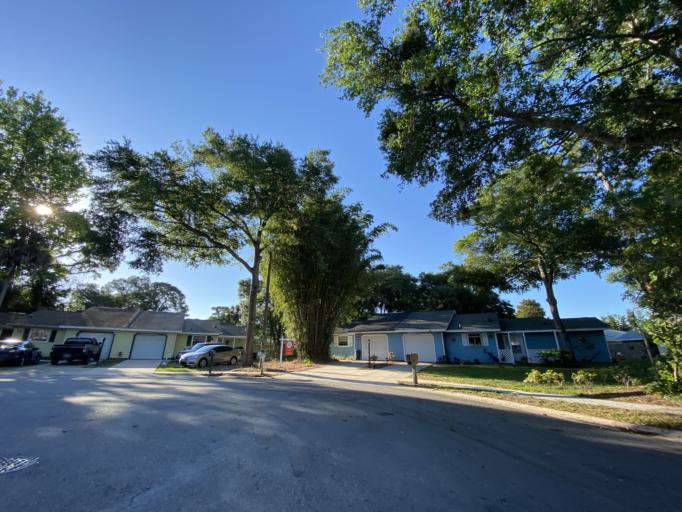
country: US
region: Florida
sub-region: Volusia County
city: Port Orange
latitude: 29.1455
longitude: -80.9997
